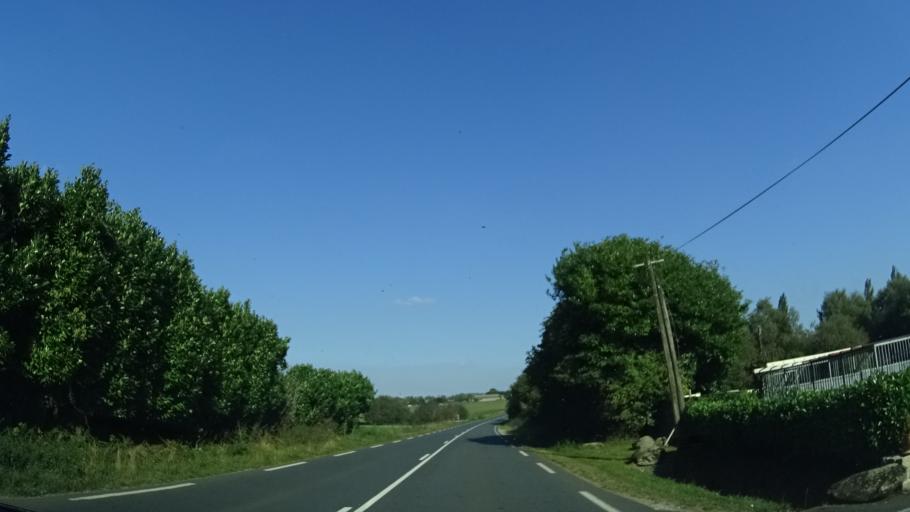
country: FR
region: Brittany
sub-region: Departement du Finistere
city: Plonevez-Porzay
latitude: 48.1276
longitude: -4.2132
